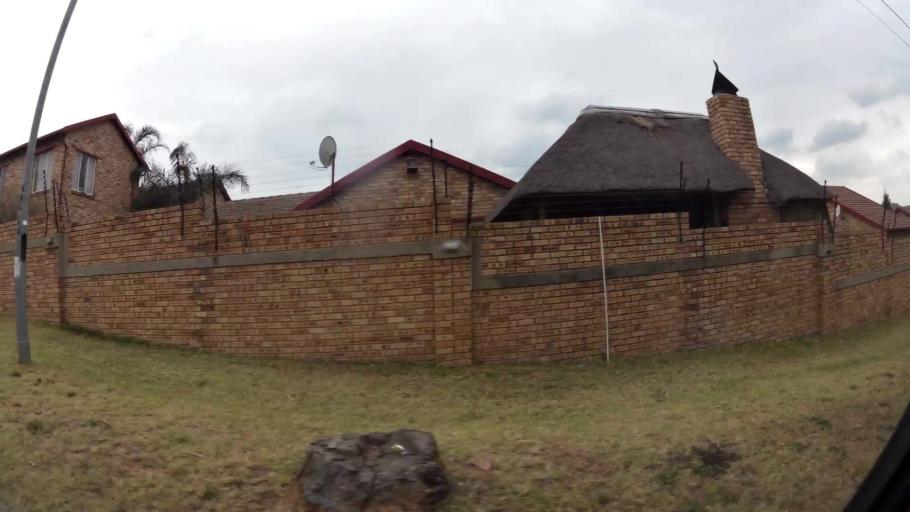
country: ZA
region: Gauteng
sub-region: City of Johannesburg Metropolitan Municipality
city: Roodepoort
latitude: -26.1092
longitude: 27.9008
